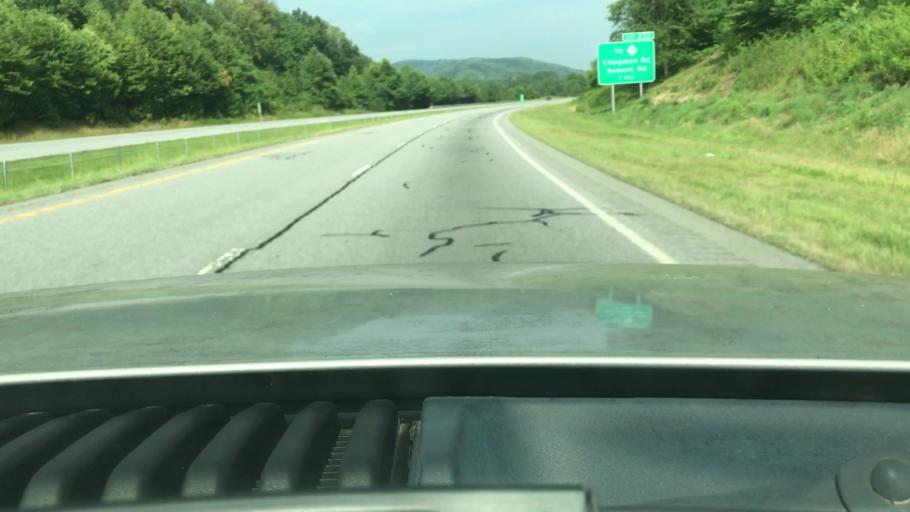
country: US
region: North Carolina
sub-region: Yadkin County
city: Jonesville
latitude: 36.1464
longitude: -80.9103
